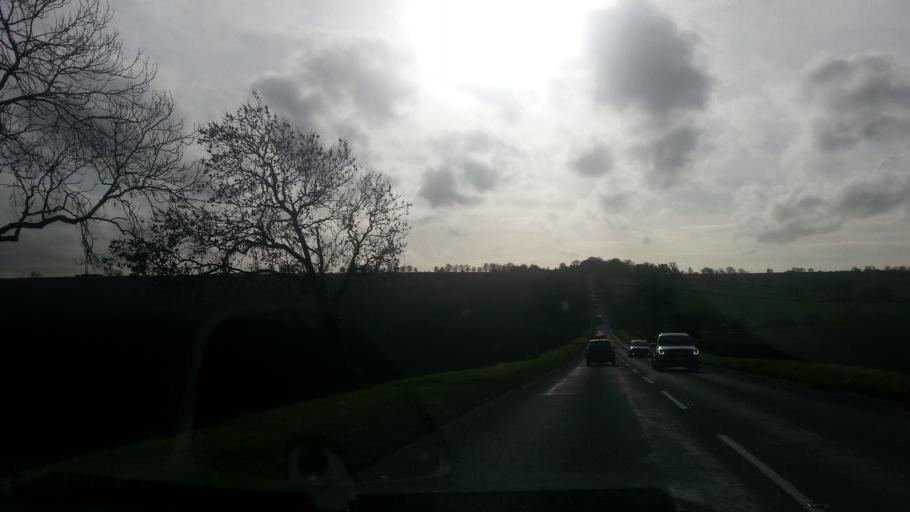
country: GB
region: England
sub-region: District of Rutland
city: Manton
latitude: 52.6268
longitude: -0.7094
